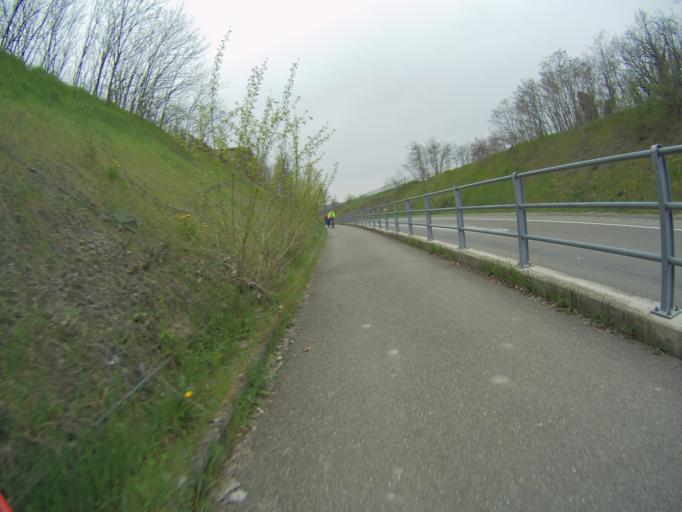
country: IT
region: Emilia-Romagna
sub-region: Provincia di Reggio Emilia
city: San Polo d'Enza
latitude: 44.6215
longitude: 10.4138
